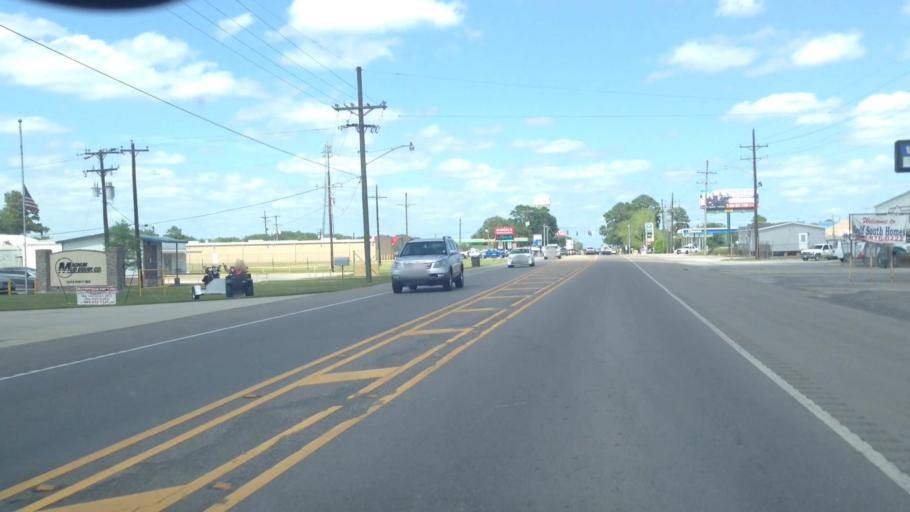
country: US
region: Louisiana
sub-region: Terrebonne Parish
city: Houma
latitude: 29.6434
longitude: -90.6893
